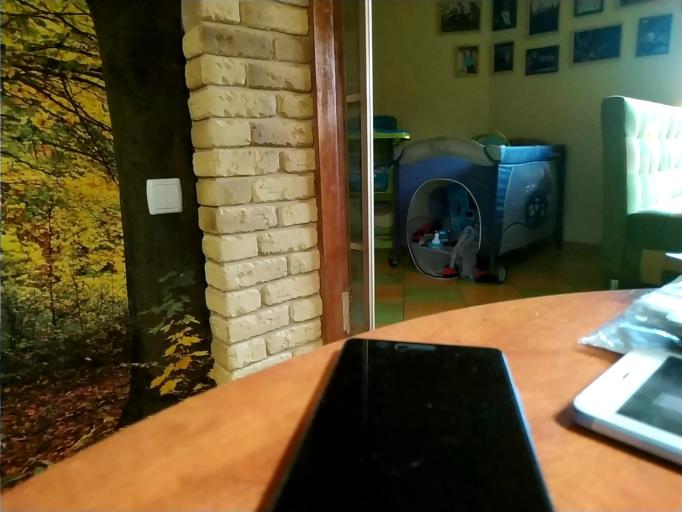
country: RU
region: Kaluga
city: Seredeyskiy
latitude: 53.7620
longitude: 35.4078
